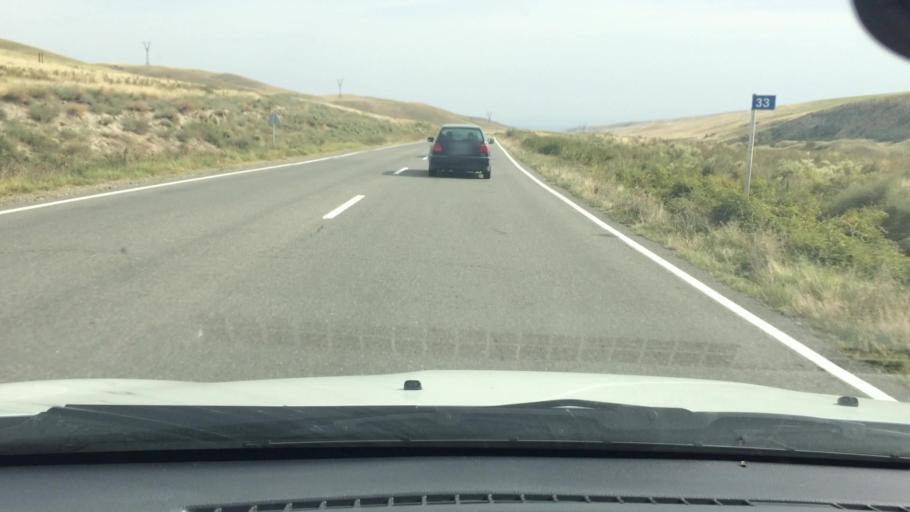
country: GE
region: Kvemo Kartli
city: Rust'avi
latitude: 41.5189
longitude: 44.9412
